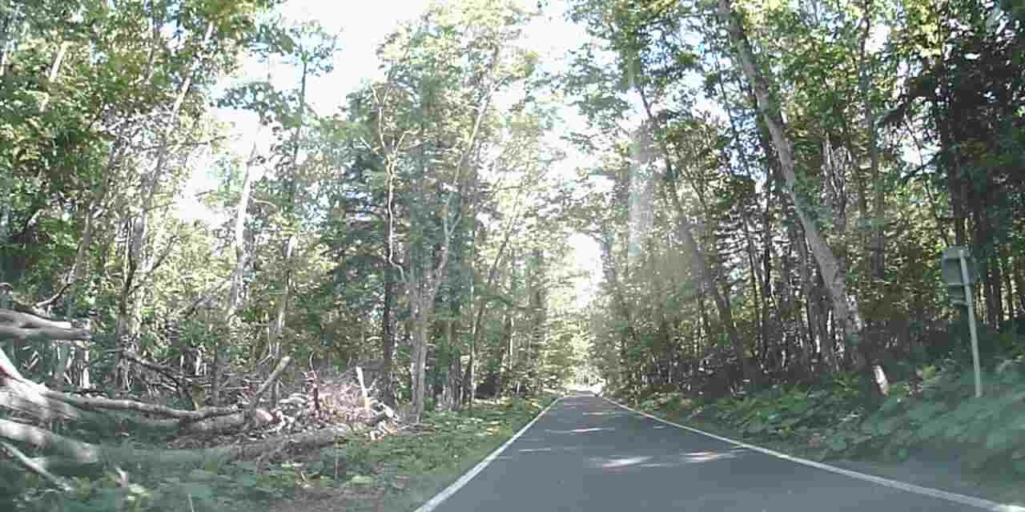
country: JP
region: Hokkaido
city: Shiraoi
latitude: 42.7312
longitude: 141.4129
